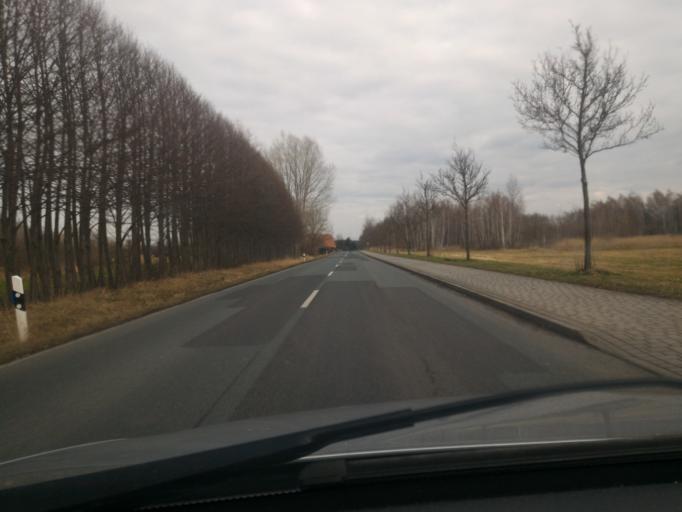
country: DE
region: Saxony
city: Zittau
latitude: 50.8675
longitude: 14.8051
